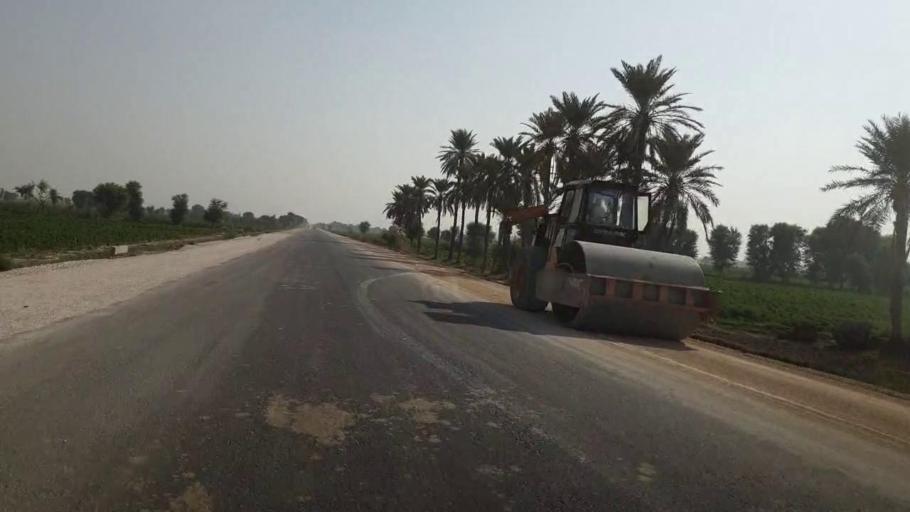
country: PK
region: Sindh
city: Bhan
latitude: 26.5462
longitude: 67.7869
